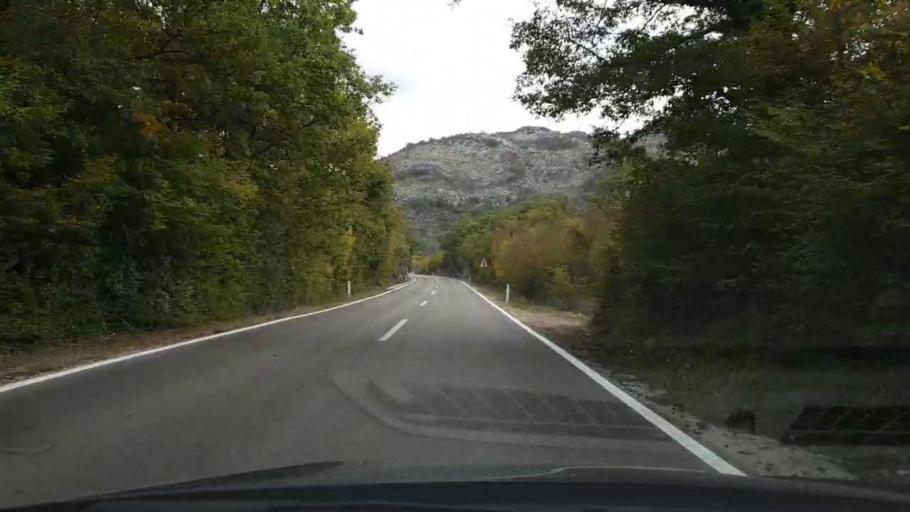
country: BA
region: Republika Srpska
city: Trebinje
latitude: 42.6856
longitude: 18.2874
